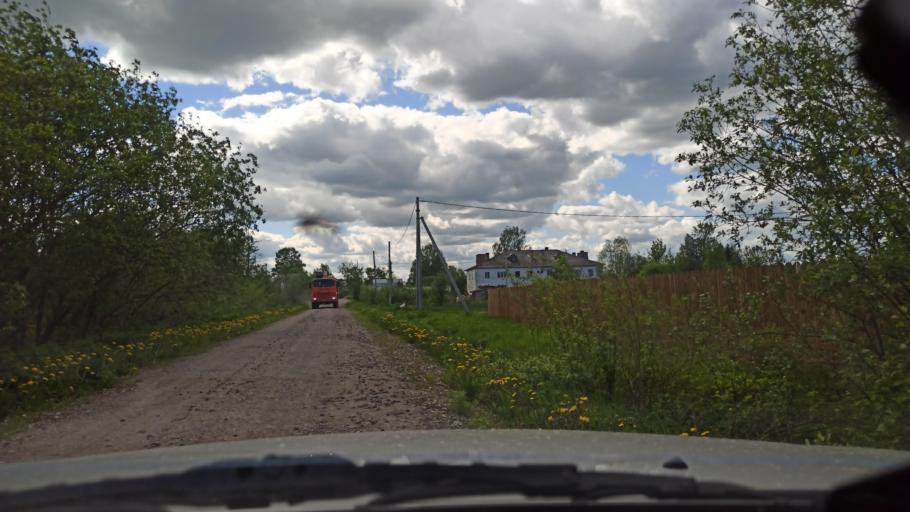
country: RU
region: Vologda
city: Vologda
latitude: 59.3435
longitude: 39.8329
